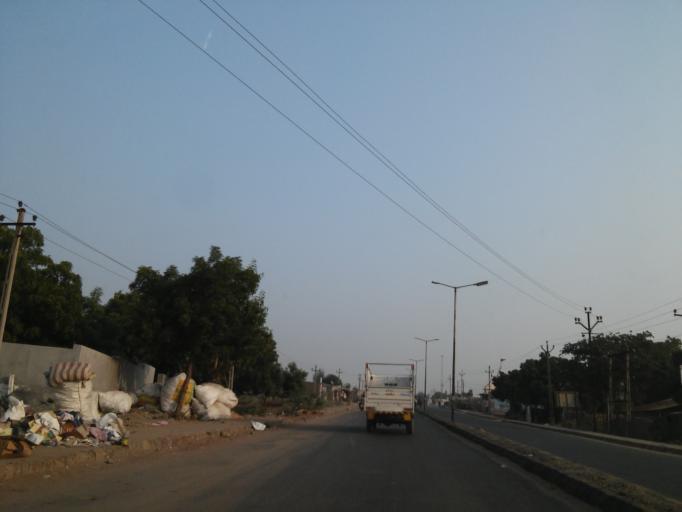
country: IN
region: Gujarat
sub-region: Kachchh
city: Bhachau
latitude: 23.2944
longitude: 70.3483
